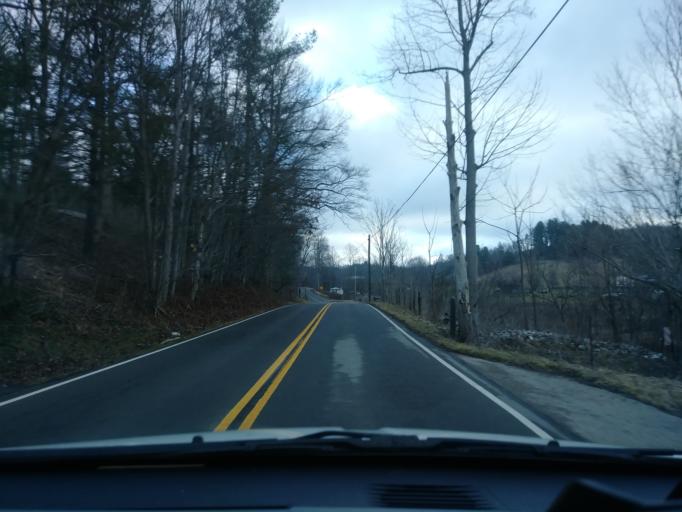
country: US
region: Tennessee
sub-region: Unicoi County
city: Unicoi
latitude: 36.1901
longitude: -82.2486
